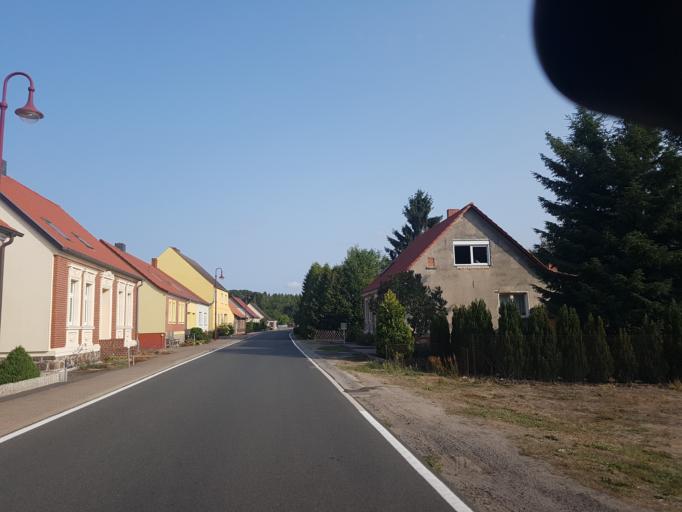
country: DE
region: Brandenburg
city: Wiesenburg
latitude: 52.0673
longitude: 12.3848
